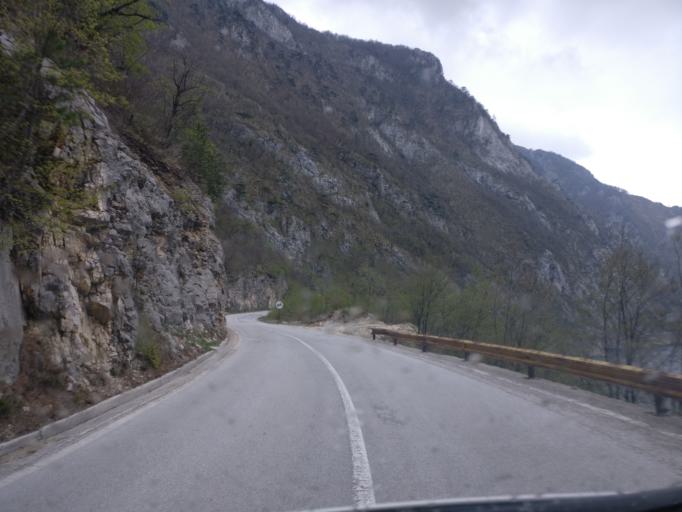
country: ME
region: Opstina Pluzine
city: Pluzine
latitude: 43.2127
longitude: 18.8577
